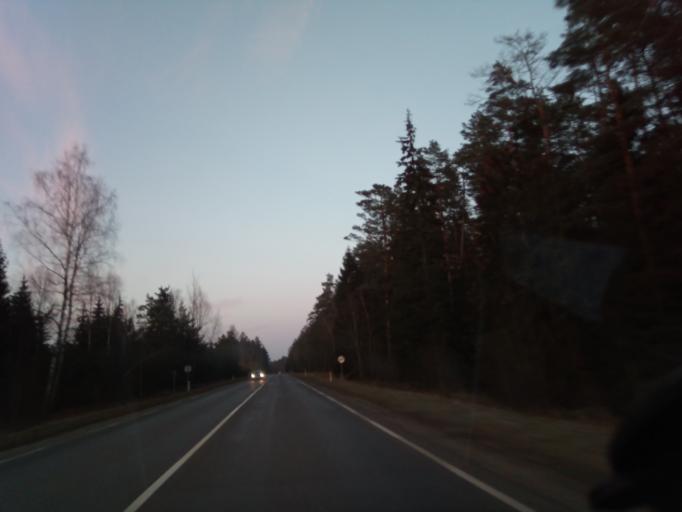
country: LT
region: Vilnius County
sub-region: Trakai
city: Rudiskes
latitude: 54.4122
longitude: 24.9767
